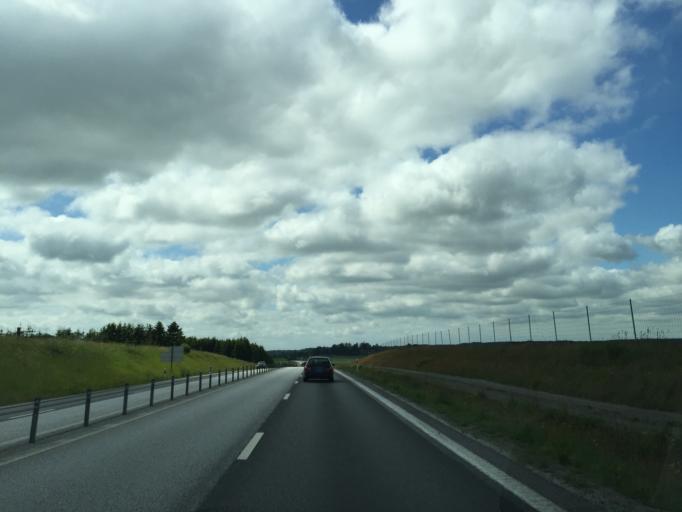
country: SE
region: Skane
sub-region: Trelleborgs Kommun
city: Anderslov
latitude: 55.5009
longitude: 13.3834
